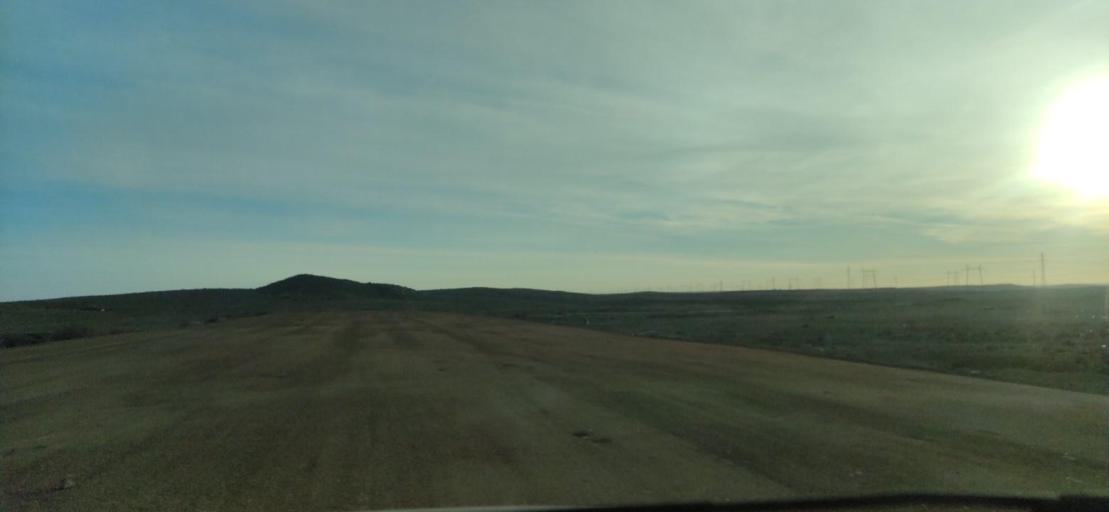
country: KZ
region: Qaraghandy
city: Saryshaghan
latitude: 46.1188
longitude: 73.5948
